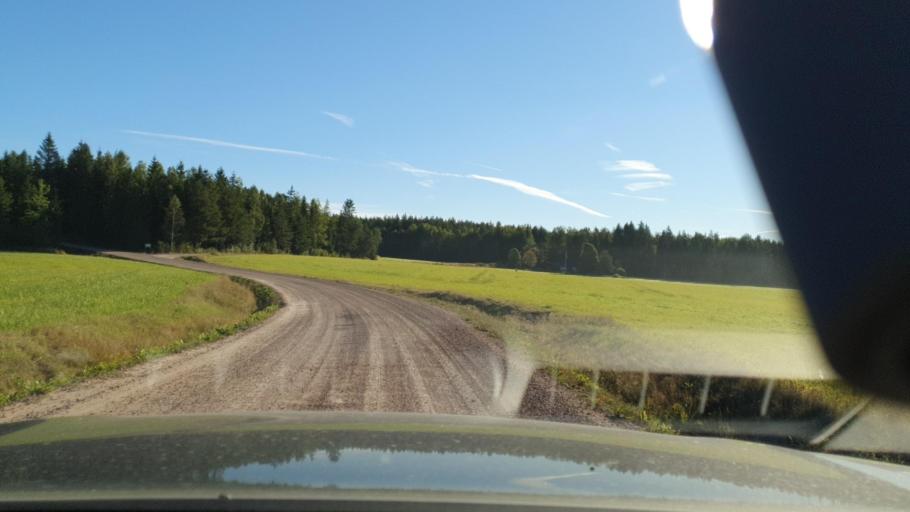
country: SE
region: Vaermland
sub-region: Karlstads Kommun
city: Molkom
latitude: 59.4461
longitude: 13.8720
